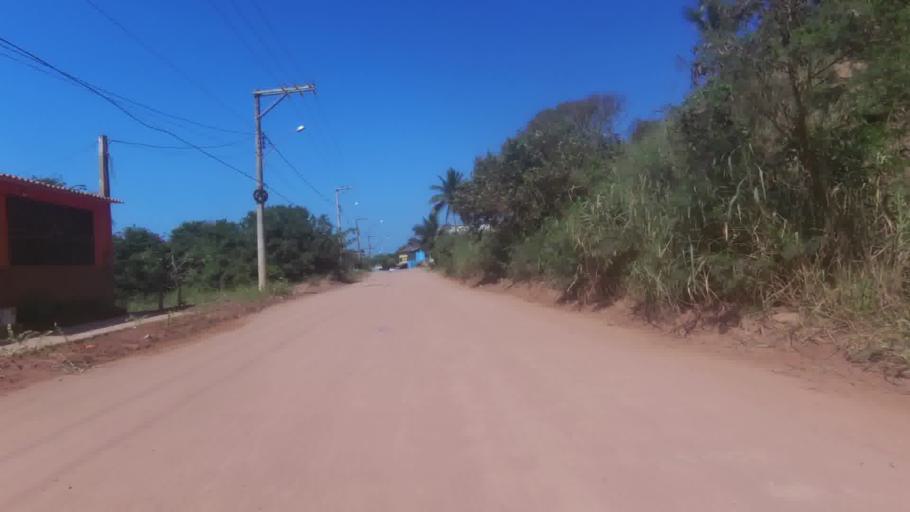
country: BR
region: Espirito Santo
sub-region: Marataizes
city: Marataizes
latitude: -21.0872
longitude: -40.8445
